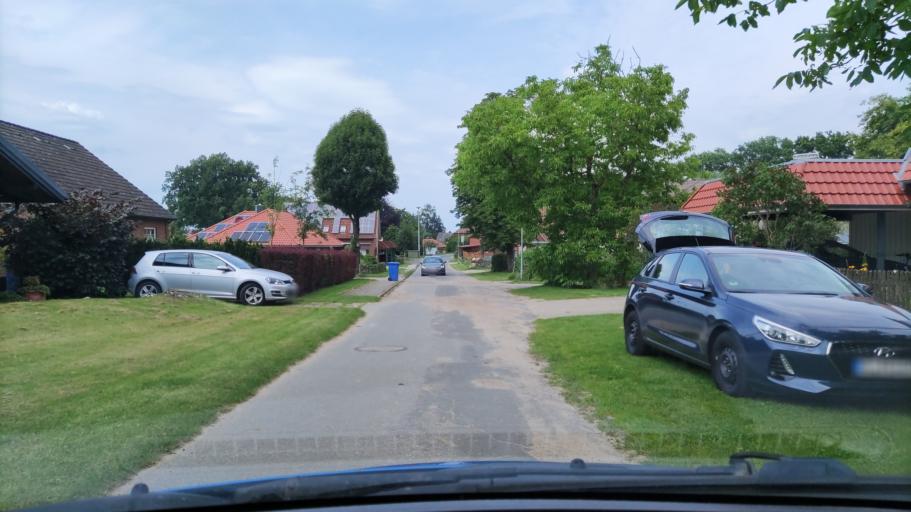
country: DE
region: Lower Saxony
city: Hanstedt
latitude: 53.2355
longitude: 10.0274
